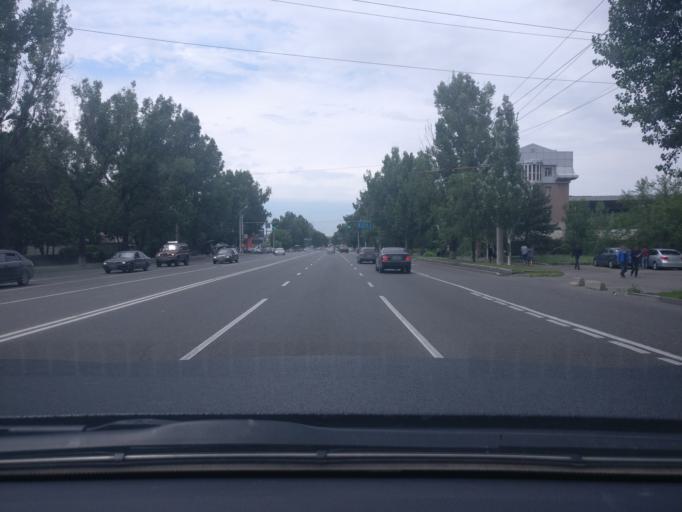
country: KZ
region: Almaty Qalasy
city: Almaty
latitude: 43.2425
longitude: 76.8577
